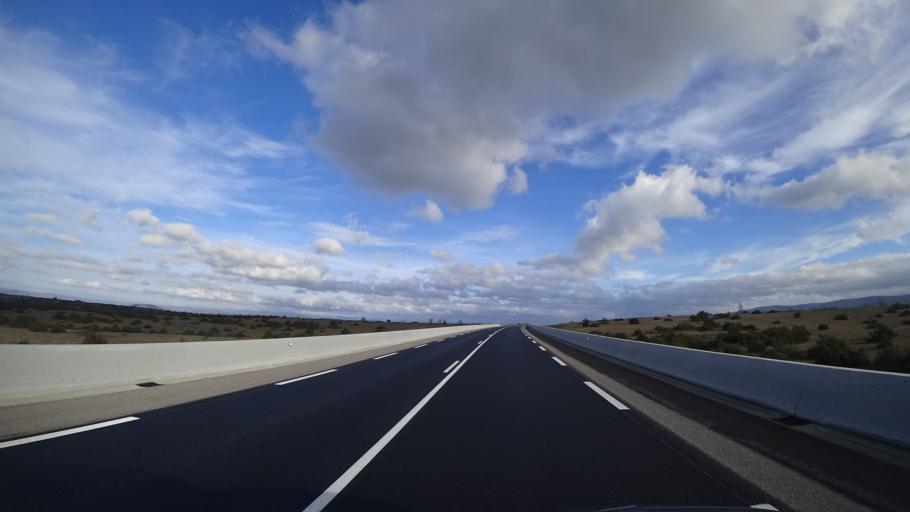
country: FR
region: Midi-Pyrenees
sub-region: Departement de l'Aveyron
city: Sebazac-Concoures
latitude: 44.4161
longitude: 2.6382
